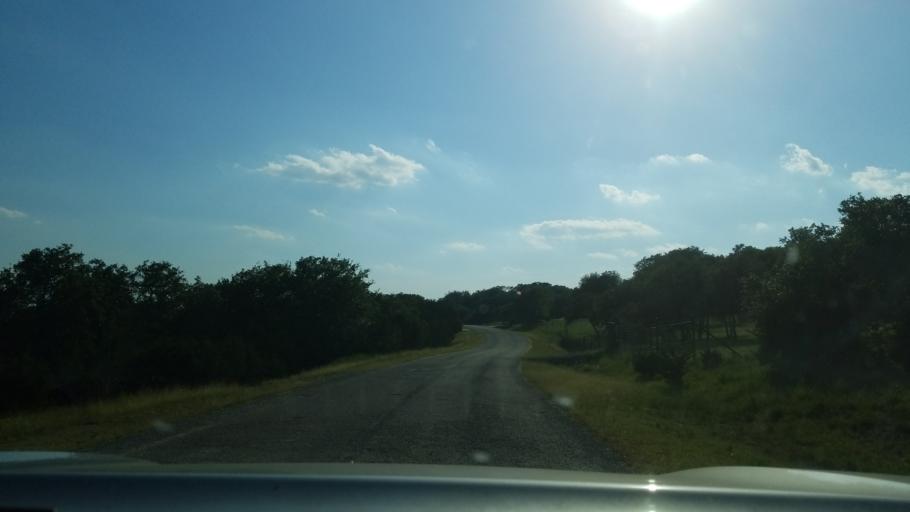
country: US
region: Texas
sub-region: Comal County
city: Bulverde
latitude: 29.7768
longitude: -98.4397
